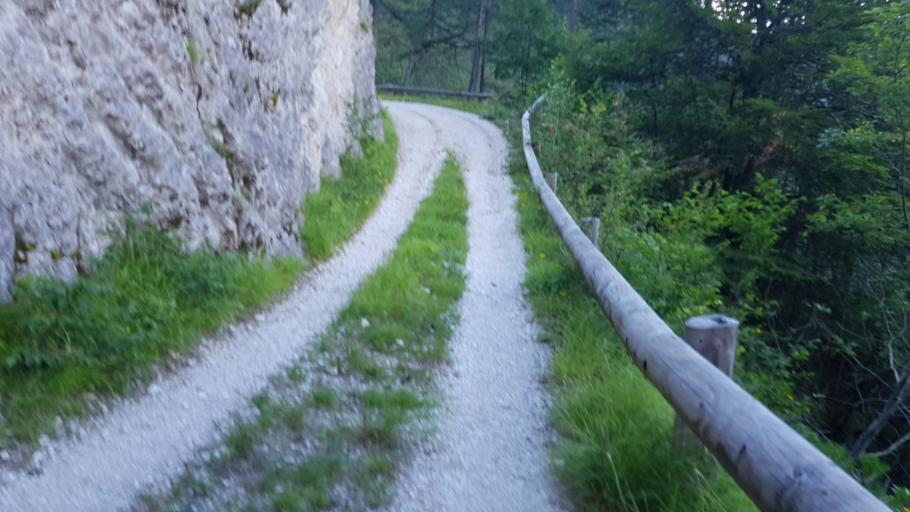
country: IT
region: Friuli Venezia Giulia
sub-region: Provincia di Udine
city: Dogna
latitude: 46.4325
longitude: 13.3038
